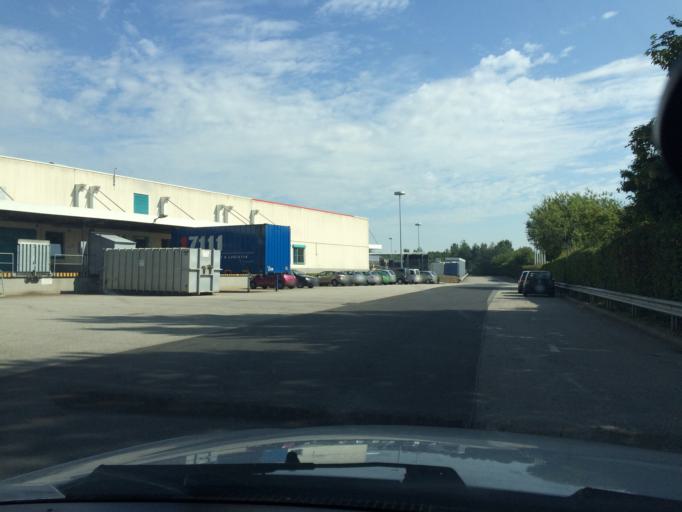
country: DE
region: Schleswig-Holstein
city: Flensburg
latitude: 54.7600
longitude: 9.4309
